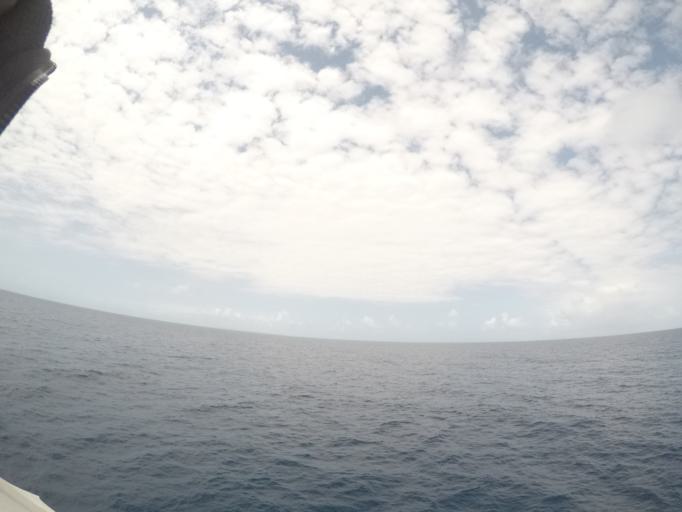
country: TZ
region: Zanzibar North
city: Nungwi
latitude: -5.6048
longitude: 39.3382
